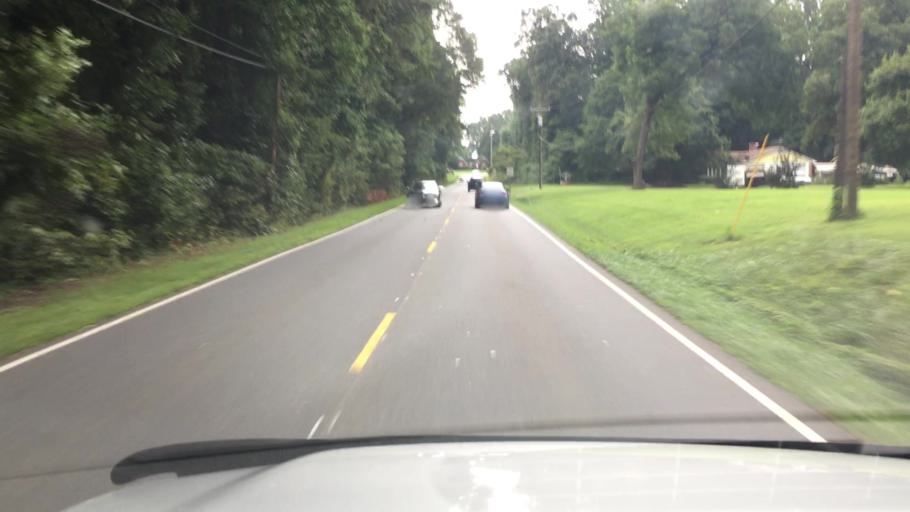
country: US
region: North Carolina
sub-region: Mecklenburg County
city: Huntersville
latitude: 35.3555
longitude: -80.8916
